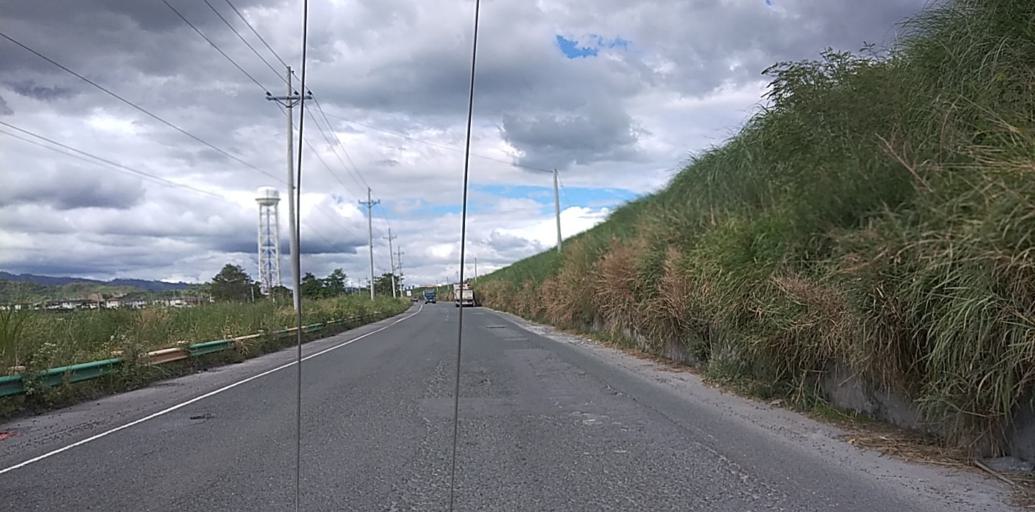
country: PH
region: Central Luzon
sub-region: Province of Pampanga
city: Dolores
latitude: 15.1097
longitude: 120.5188
